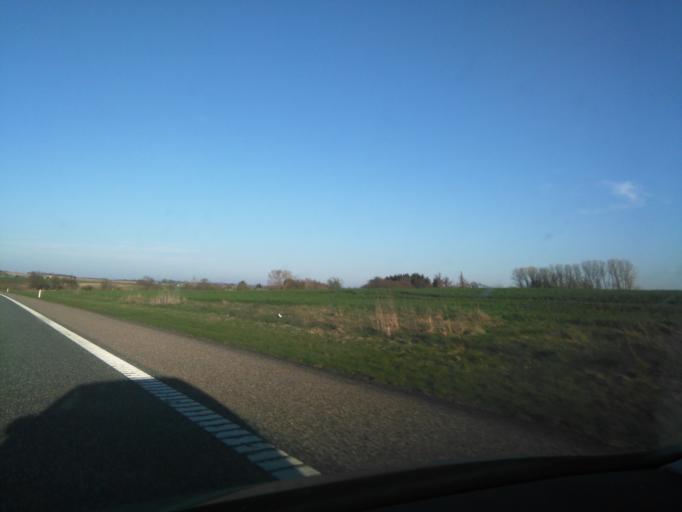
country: DK
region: Central Jutland
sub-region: Skanderborg Kommune
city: Galten
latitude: 56.1434
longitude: 9.8858
